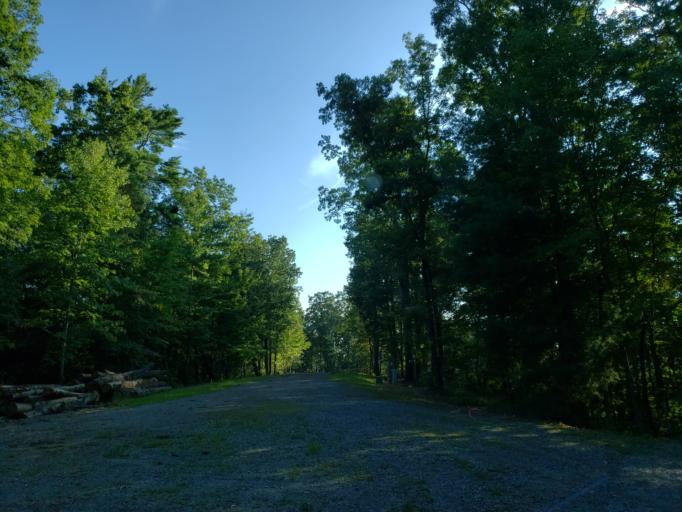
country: US
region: Georgia
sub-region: Fannin County
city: Blue Ridge
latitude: 34.6921
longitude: -84.2775
